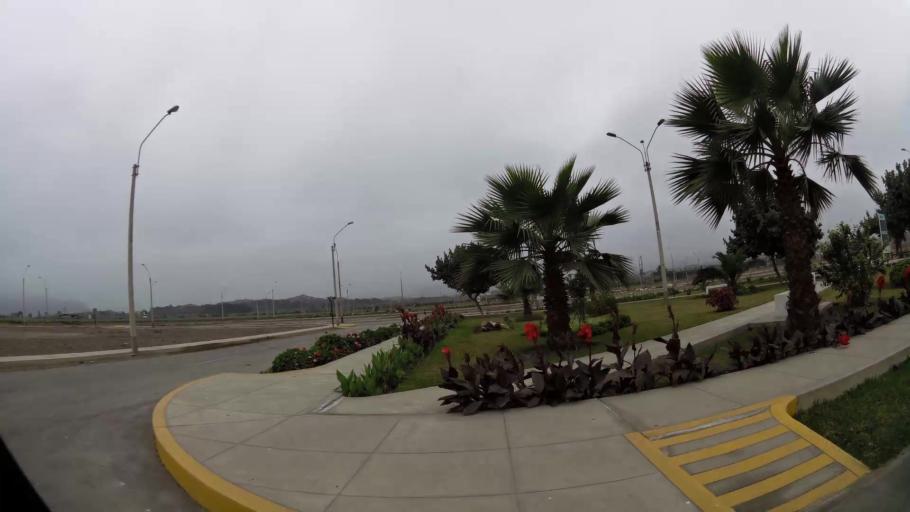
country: PE
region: Lima
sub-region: Barranca
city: Barranca
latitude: -10.7396
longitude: -77.7615
